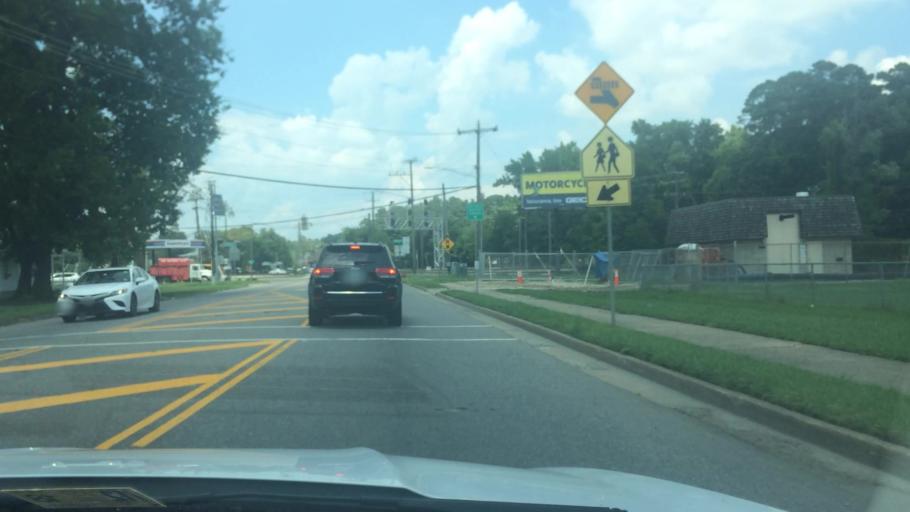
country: US
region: Virginia
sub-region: York County
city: Yorktown
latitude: 37.1907
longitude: -76.5716
